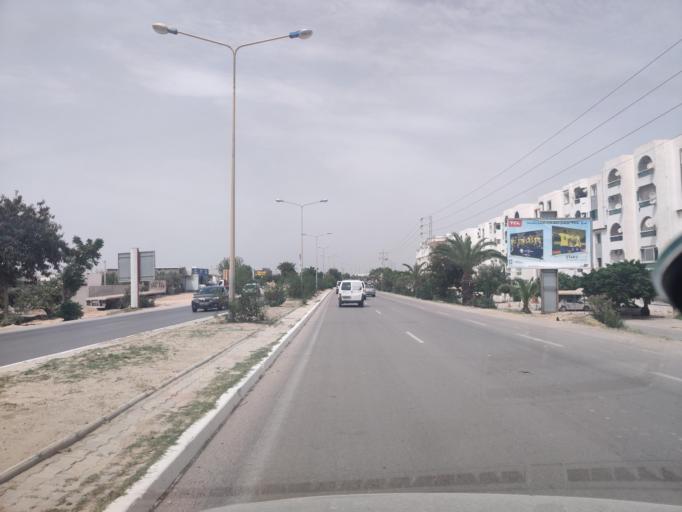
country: TN
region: Susah
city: Hammam Sousse
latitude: 35.8378
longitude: 10.5857
